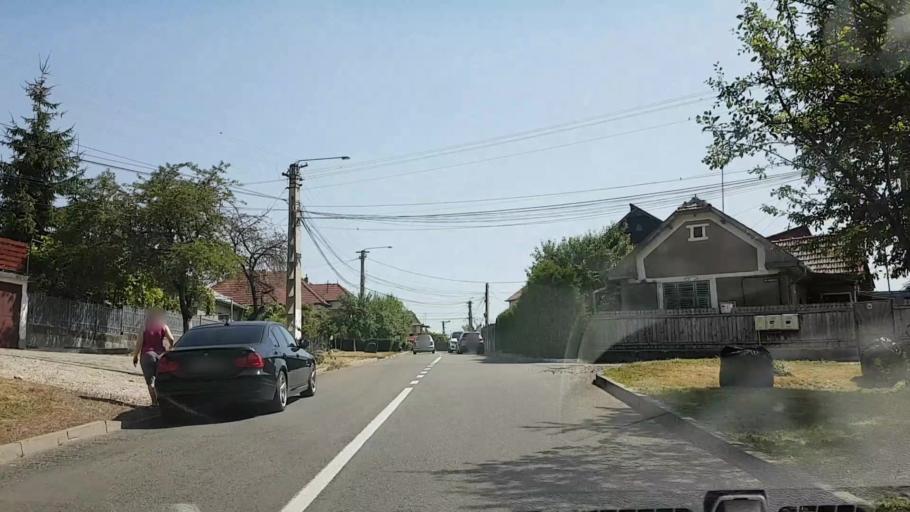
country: RO
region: Cluj
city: Turda
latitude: 46.5785
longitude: 23.7926
